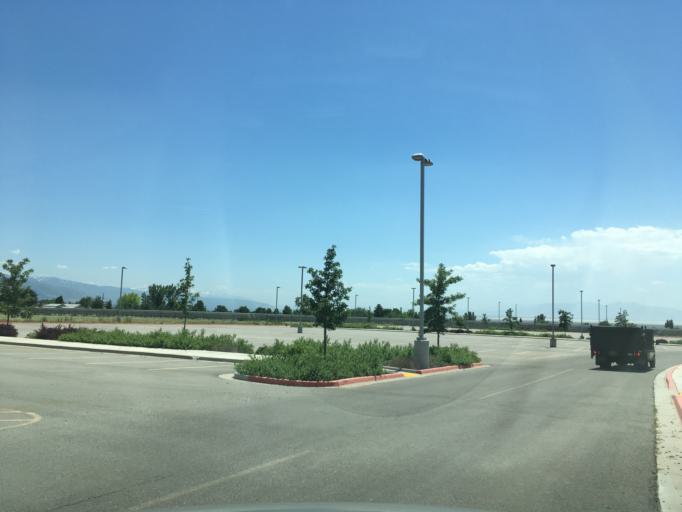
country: US
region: Utah
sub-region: Davis County
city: Hill Air Force Bace
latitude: 41.0989
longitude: -111.9798
